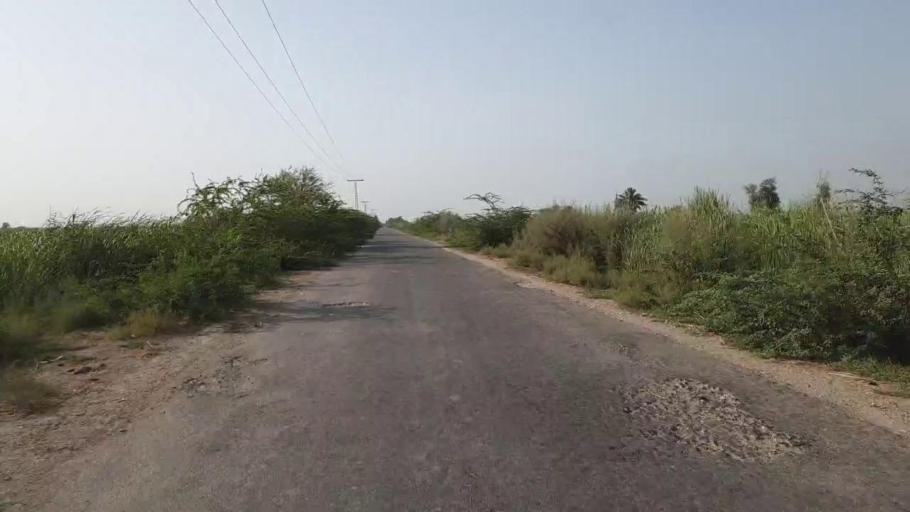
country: PK
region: Sindh
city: Jam Sahib
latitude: 26.3983
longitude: 68.8784
